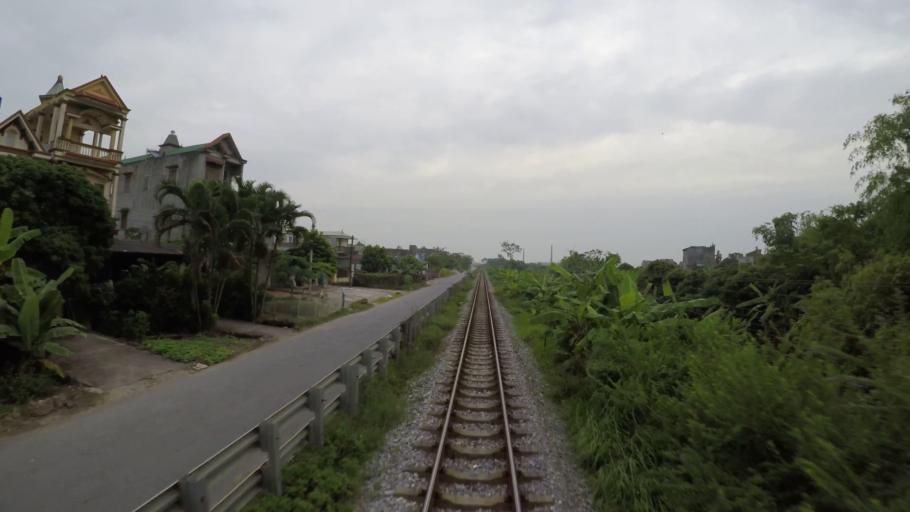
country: VN
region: Hung Yen
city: Ban Yen Nhan
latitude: 20.9655
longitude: 106.1113
